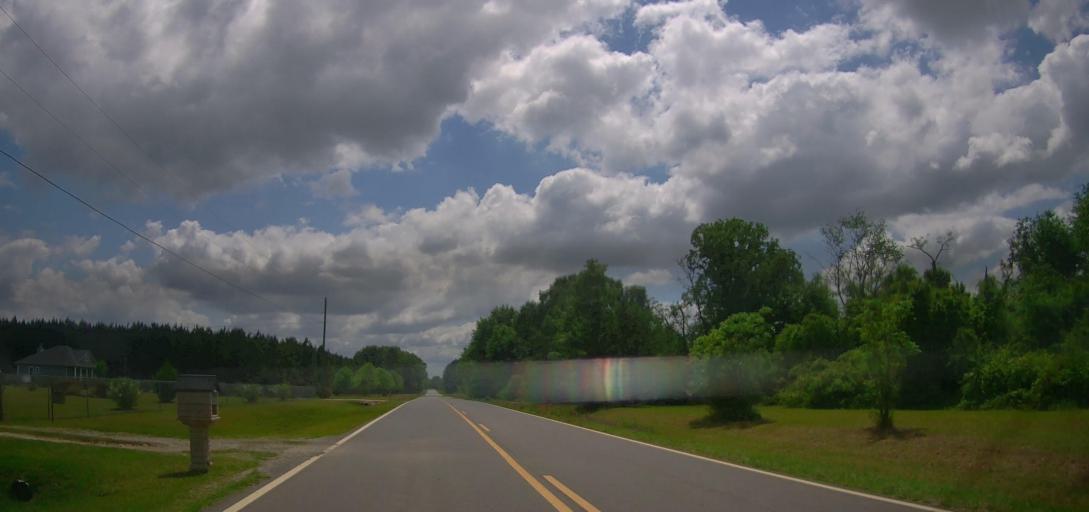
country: US
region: Georgia
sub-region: Laurens County
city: Dublin
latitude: 32.5981
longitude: -82.9547
